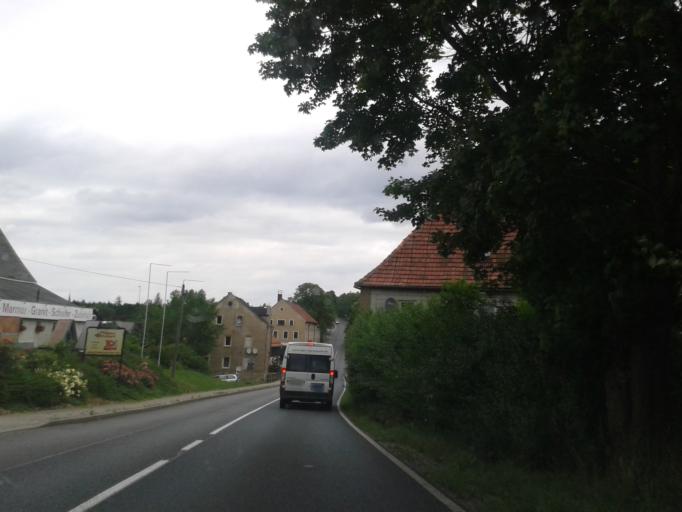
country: DE
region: Saxony
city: Niederschona
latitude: 50.9612
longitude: 13.4224
